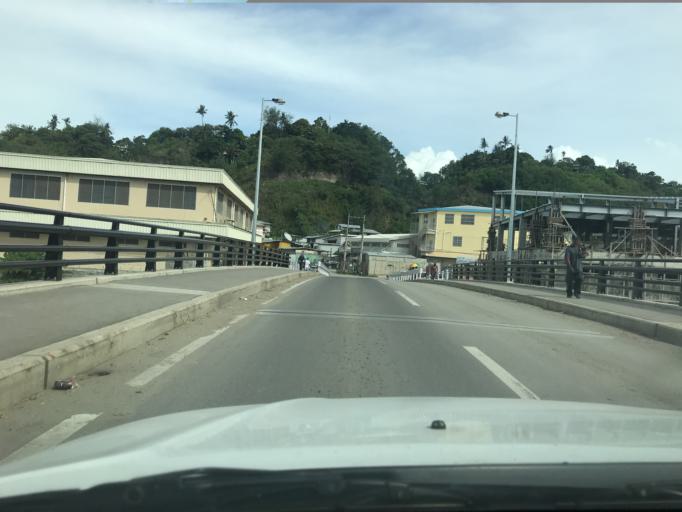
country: SB
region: Guadalcanal
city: Honiara
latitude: -9.4383
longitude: 159.9638
